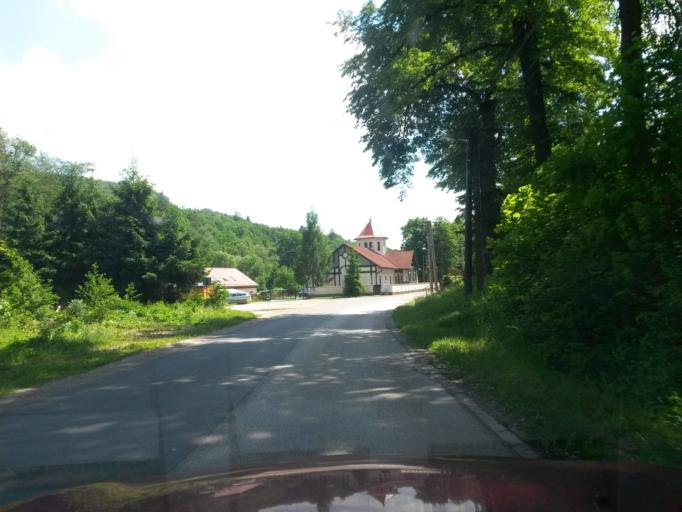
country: SK
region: Kosicky
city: Roznava
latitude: 48.6797
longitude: 20.5427
